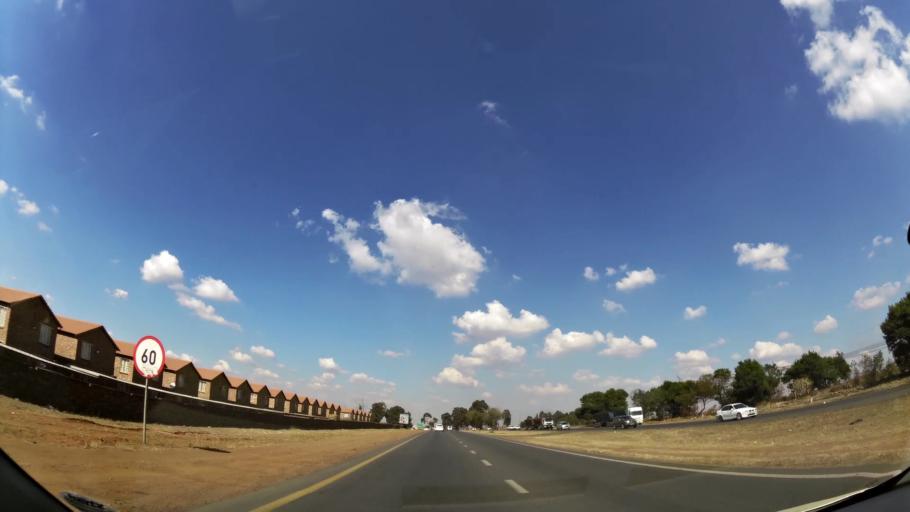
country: ZA
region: Mpumalanga
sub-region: Nkangala District Municipality
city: Witbank
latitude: -25.9492
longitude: 29.2474
